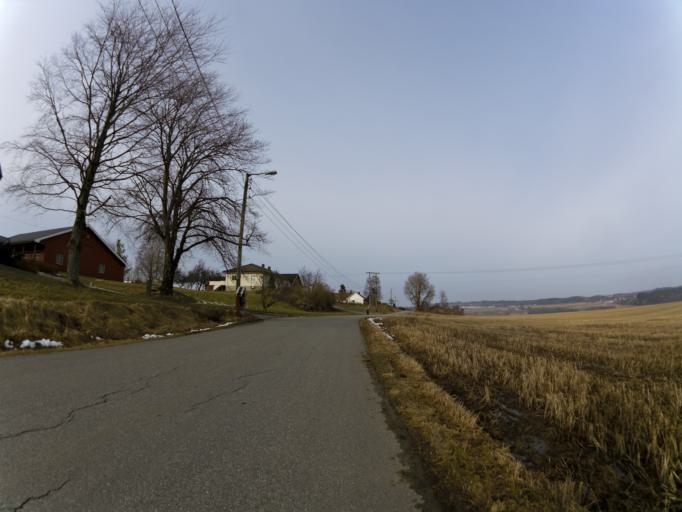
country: NO
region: Ostfold
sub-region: Fredrikstad
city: Fredrikstad
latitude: 59.2806
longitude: 10.9997
